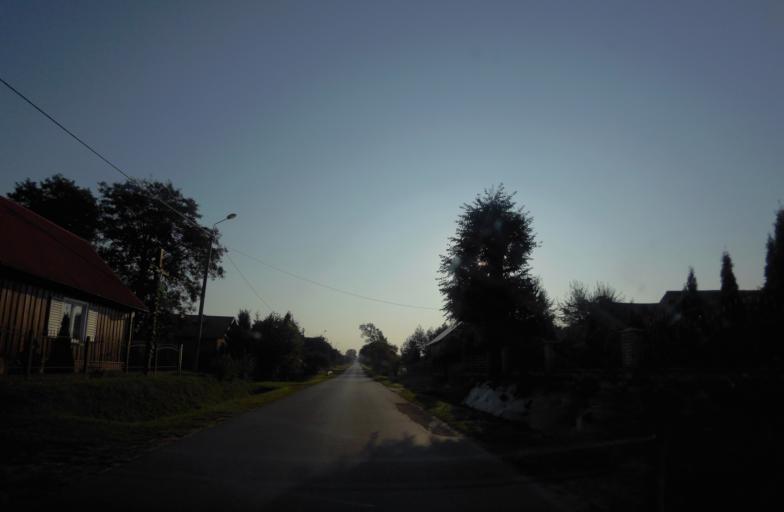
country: PL
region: Lublin Voivodeship
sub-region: Powiat janowski
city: Dzwola
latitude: 50.5793
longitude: 22.5514
